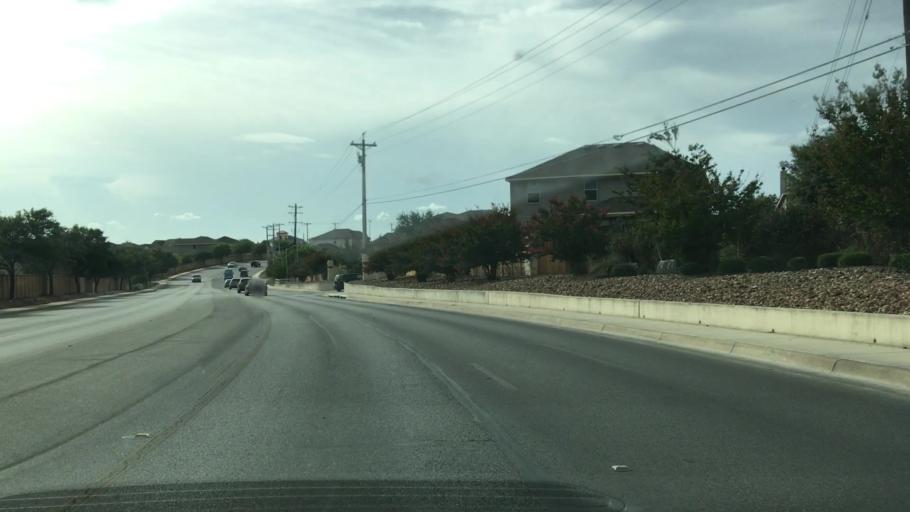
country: US
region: Texas
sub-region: Guadalupe County
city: Northcliff
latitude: 29.5973
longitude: -98.2565
